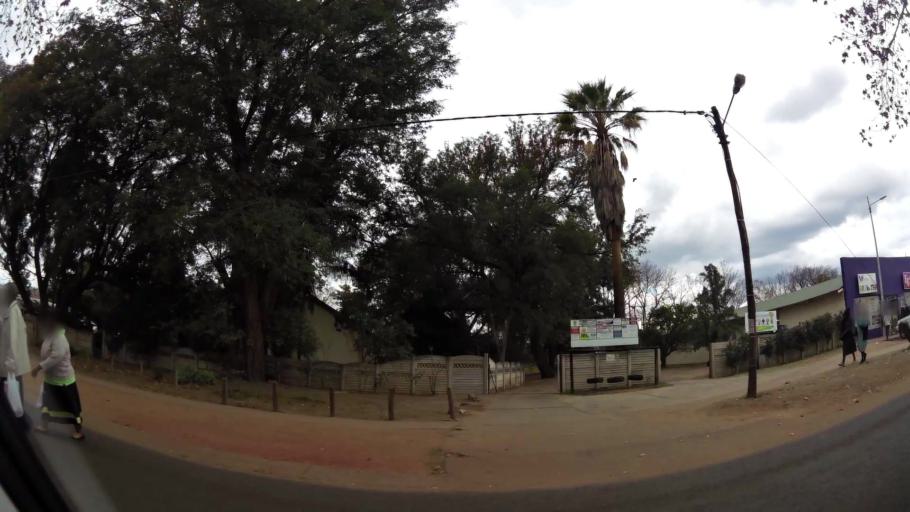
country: ZA
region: Limpopo
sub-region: Waterberg District Municipality
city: Modimolle
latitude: -24.7040
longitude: 28.4110
